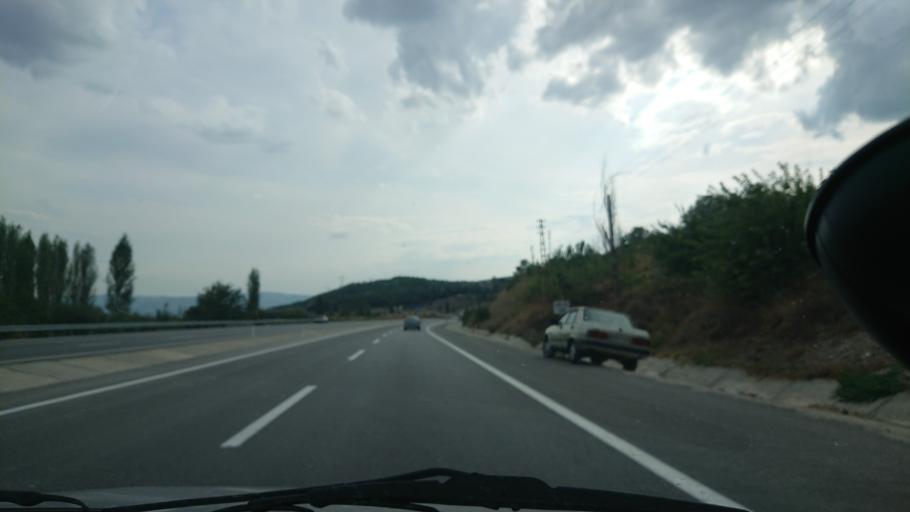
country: TR
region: Kuetahya
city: Gediz
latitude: 39.0365
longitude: 29.4205
